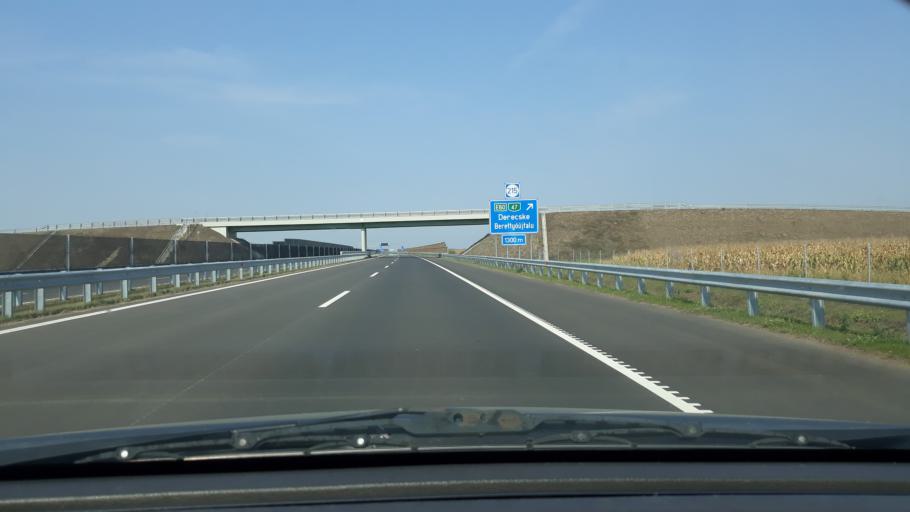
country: HU
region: Hajdu-Bihar
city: Berettyoujfalu
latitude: 47.2623
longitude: 21.5644
